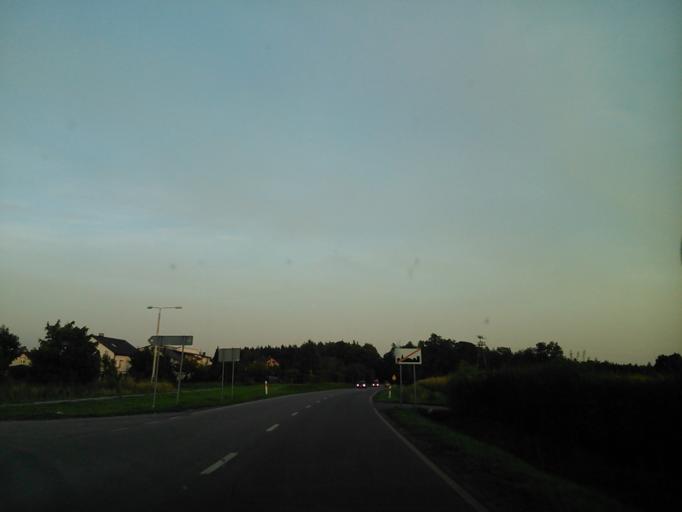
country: PL
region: Kujawsko-Pomorskie
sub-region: Powiat wabrzeski
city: Wabrzezno
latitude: 53.2634
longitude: 18.9984
